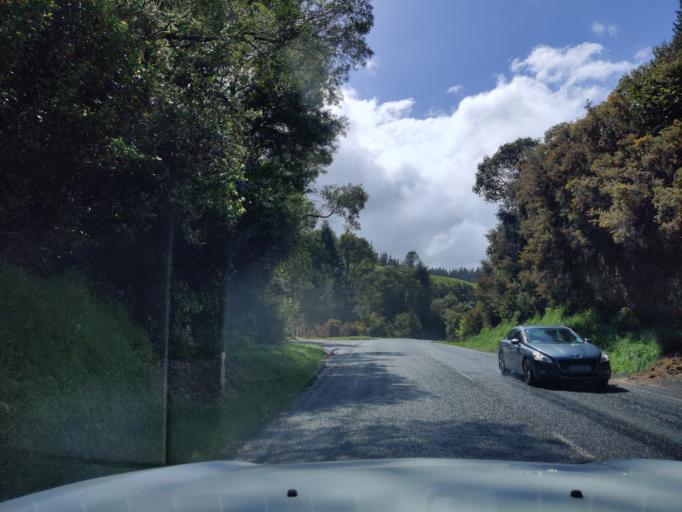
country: NZ
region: Bay of Plenty
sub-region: Rotorua District
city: Rotorua
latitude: -38.1618
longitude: 176.3019
